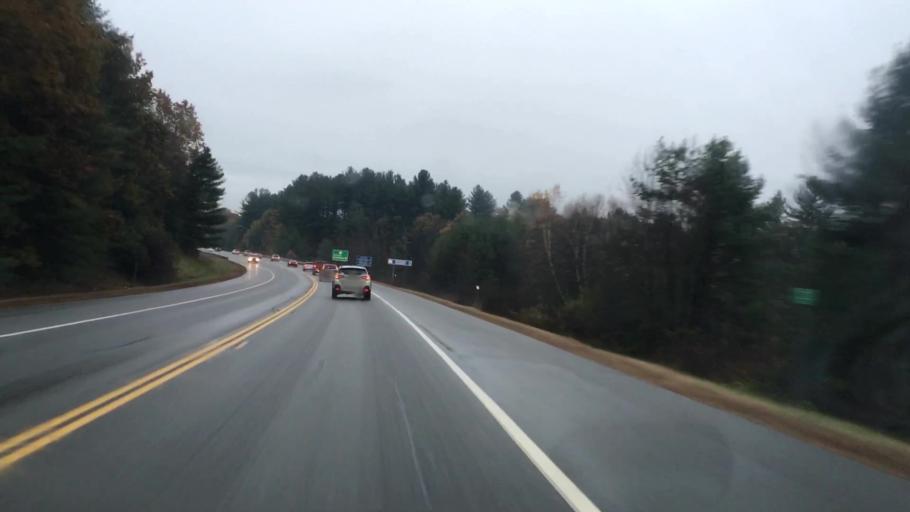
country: US
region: New Hampshire
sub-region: Hillsborough County
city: Milford
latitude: 42.8195
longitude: -71.6554
